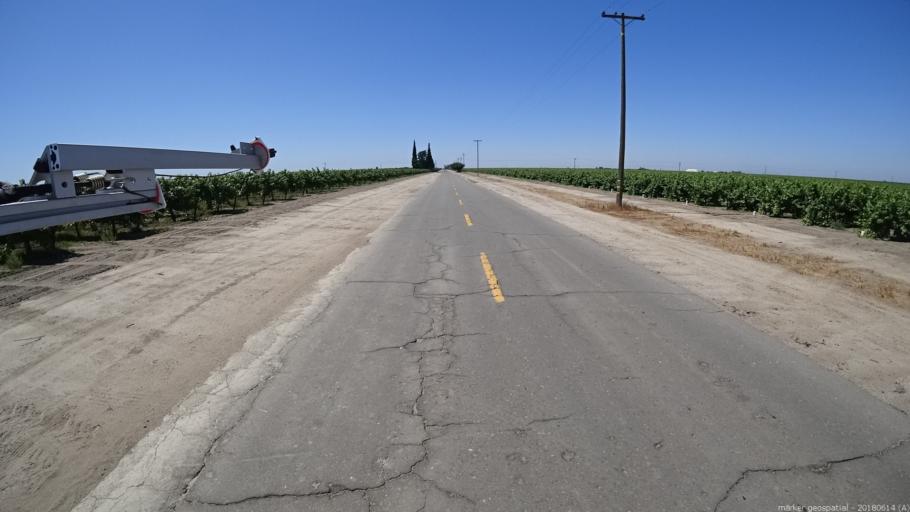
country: US
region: California
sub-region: Madera County
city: Fairmead
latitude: 36.9701
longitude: -120.1842
